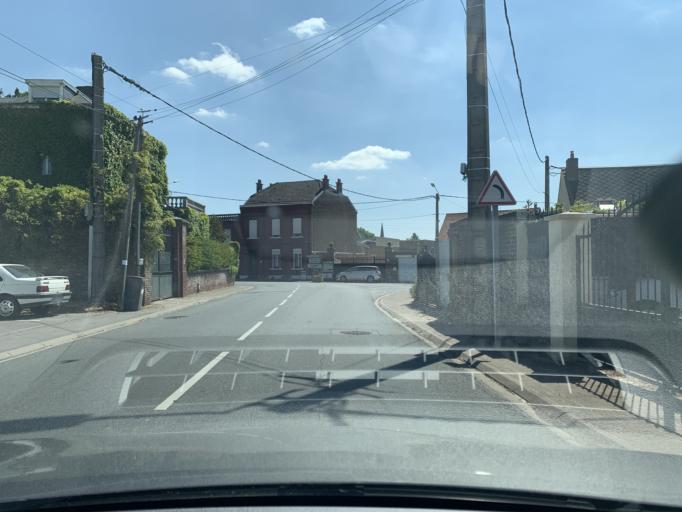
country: FR
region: Nord-Pas-de-Calais
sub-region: Departement du Nord
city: Fontaine-au-Pire
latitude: 50.1338
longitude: 3.3766
